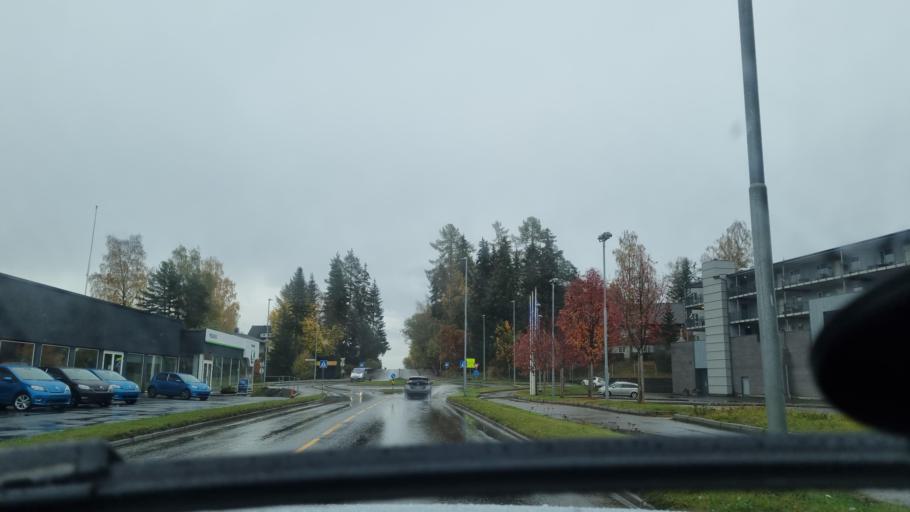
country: NO
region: Hedmark
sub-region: Hamar
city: Hamar
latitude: 60.7980
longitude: 11.0503
